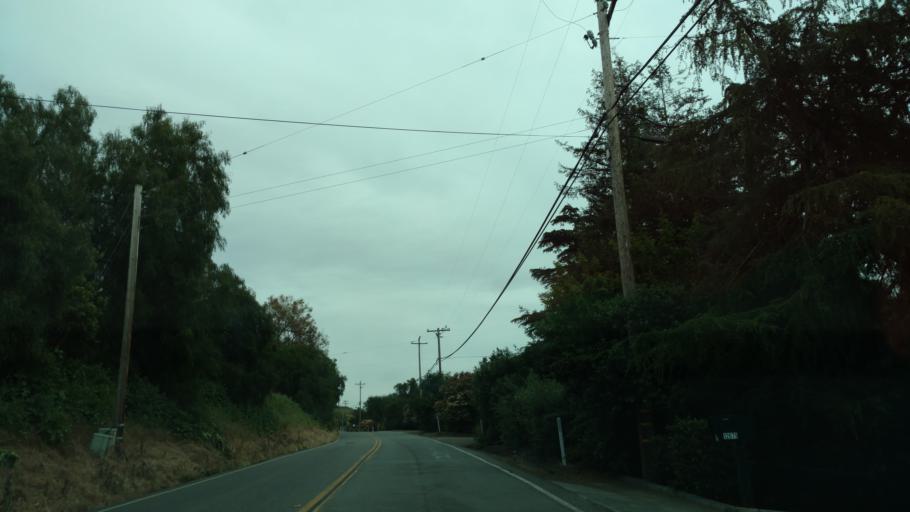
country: US
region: California
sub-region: Santa Clara County
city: East Foothills
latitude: 37.3764
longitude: -121.8010
